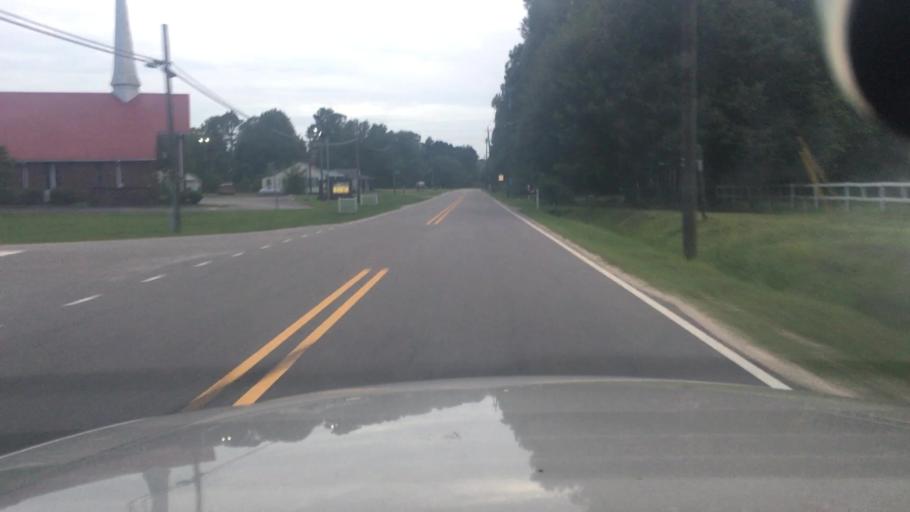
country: US
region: North Carolina
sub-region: Cumberland County
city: Hope Mills
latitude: 34.9664
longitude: -78.9280
